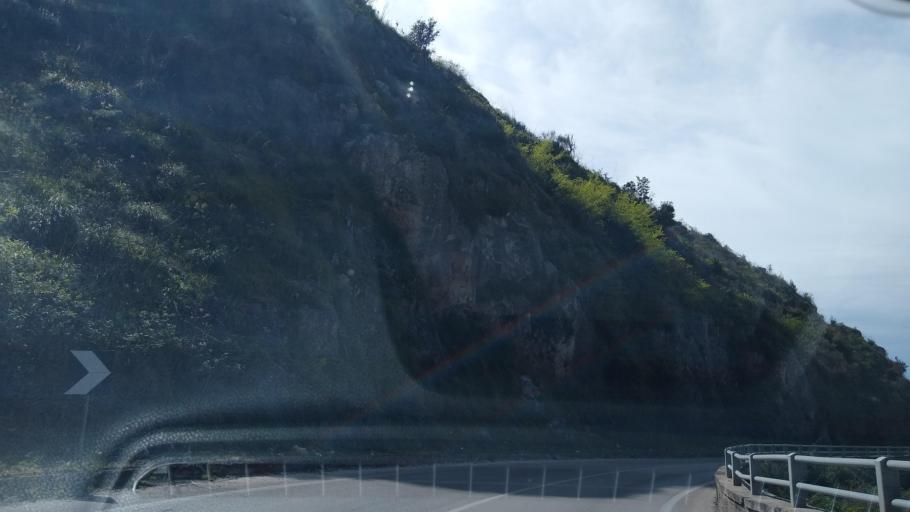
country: IT
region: Sicily
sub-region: Palermo
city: Pioppo
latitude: 38.0493
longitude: 13.1931
